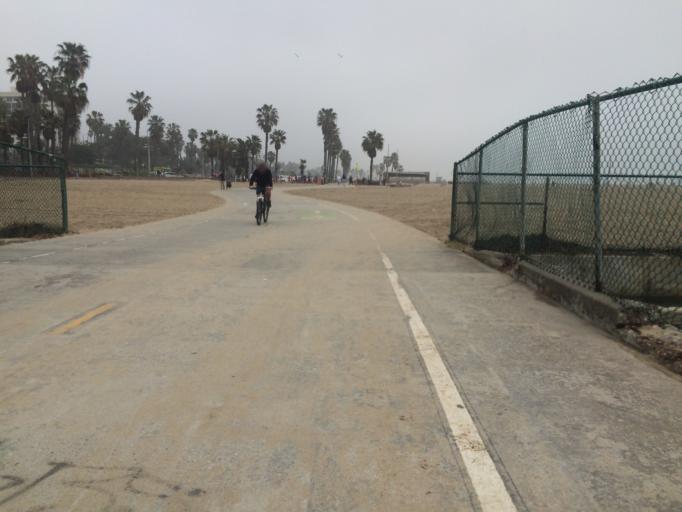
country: US
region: California
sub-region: Los Angeles County
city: Santa Monica
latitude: 34.0063
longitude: -118.4923
